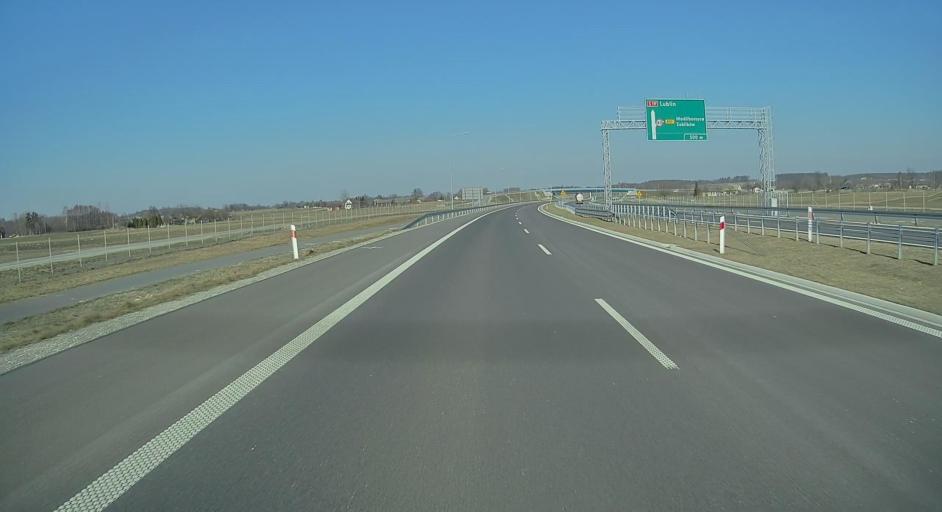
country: PL
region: Lublin Voivodeship
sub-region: Powiat janowski
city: Modliborzyce
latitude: 50.7488
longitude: 22.2946
